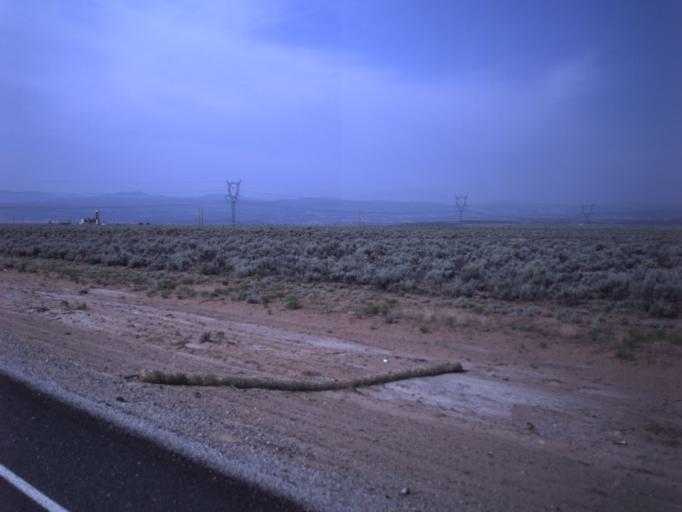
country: US
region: Utah
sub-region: Duchesne County
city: Duchesne
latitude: 40.2465
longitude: -110.3874
